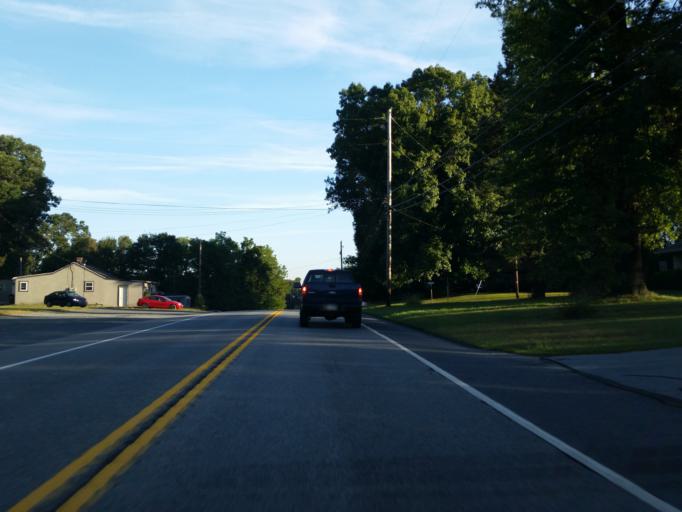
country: US
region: Pennsylvania
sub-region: Lancaster County
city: Quarryville
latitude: 39.9041
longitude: -76.2419
